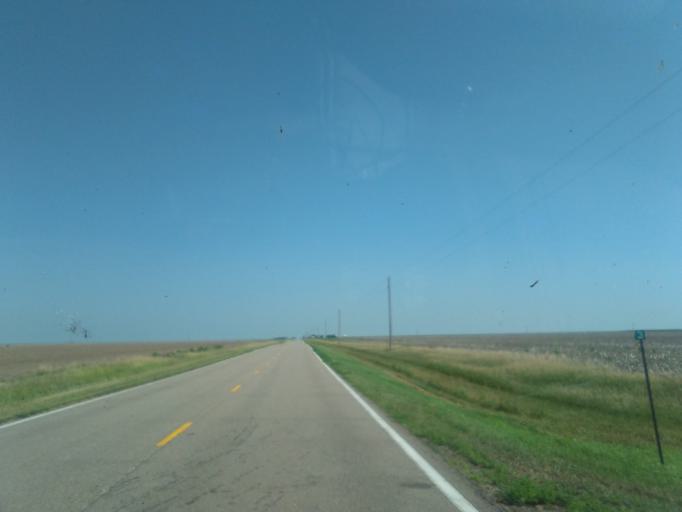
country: US
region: Nebraska
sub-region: Dundy County
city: Benkelman
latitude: 39.8004
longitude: -101.5419
